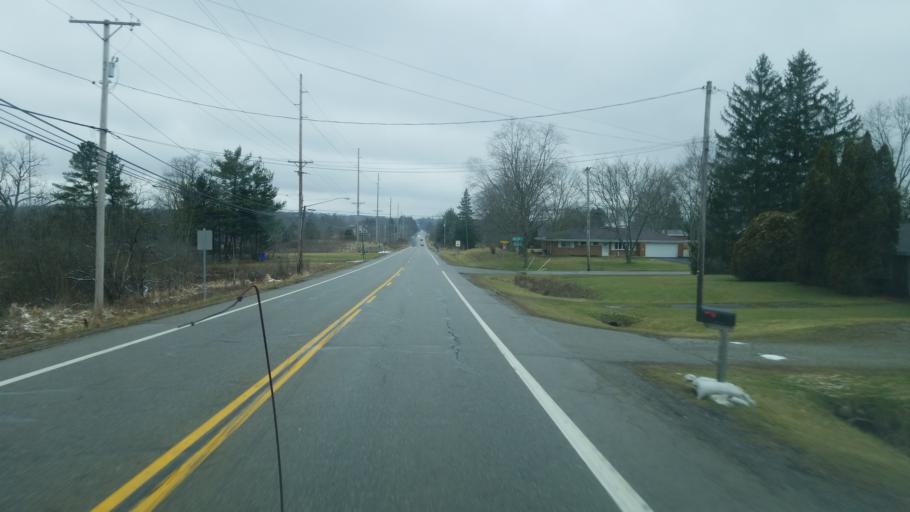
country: US
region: Ohio
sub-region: Portage County
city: Streetsboro
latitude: 41.2397
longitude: -81.3573
